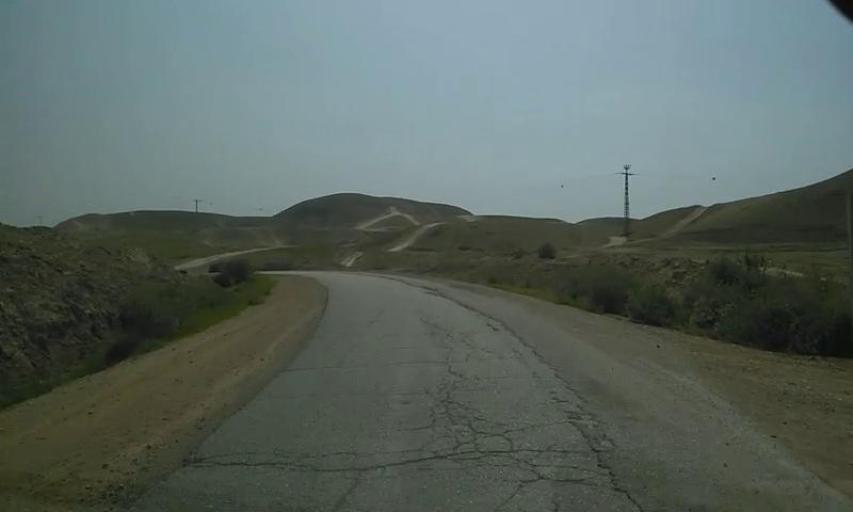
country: PS
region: West Bank
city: Jericho
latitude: 31.7963
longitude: 35.4267
